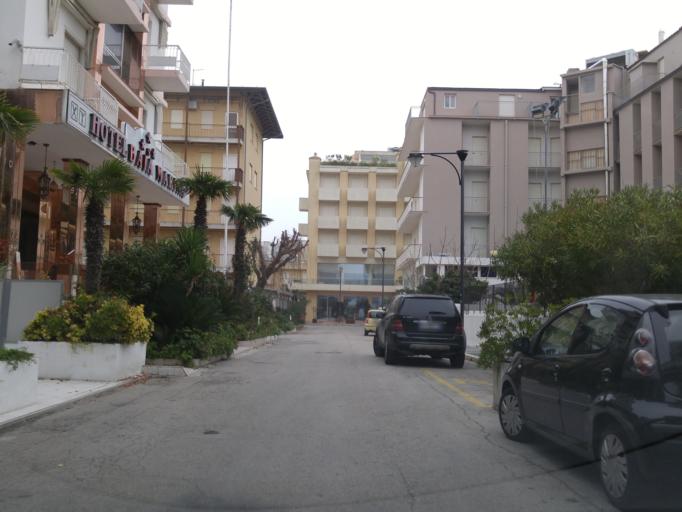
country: IT
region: Emilia-Romagna
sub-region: Provincia di Rimini
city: Cattolica
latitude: 43.9695
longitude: 12.7272
